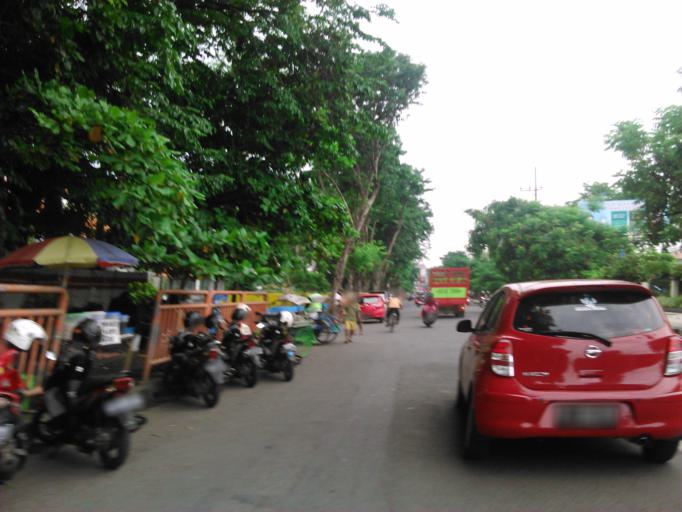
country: ID
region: East Java
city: Gubengairlangga
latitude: -7.2706
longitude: 112.7595
